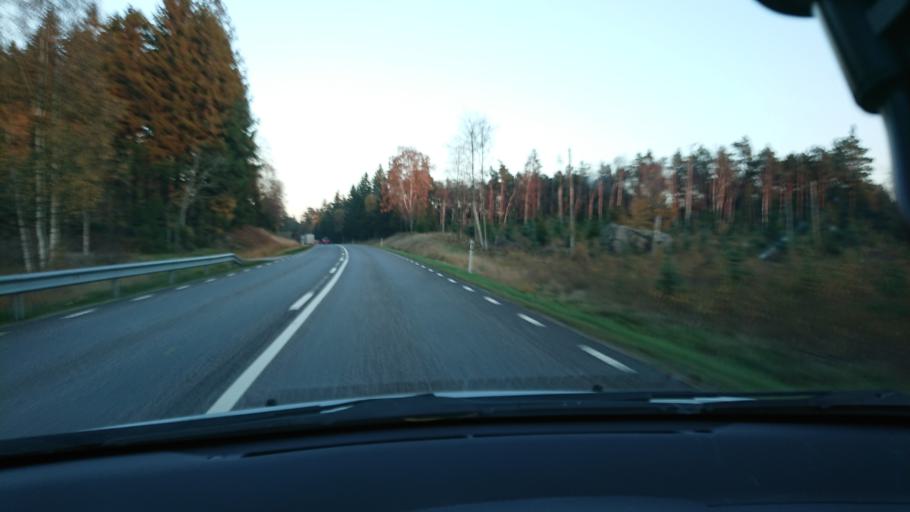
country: SE
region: Halland
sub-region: Laholms Kommun
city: Knared
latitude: 56.7122
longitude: 13.2577
